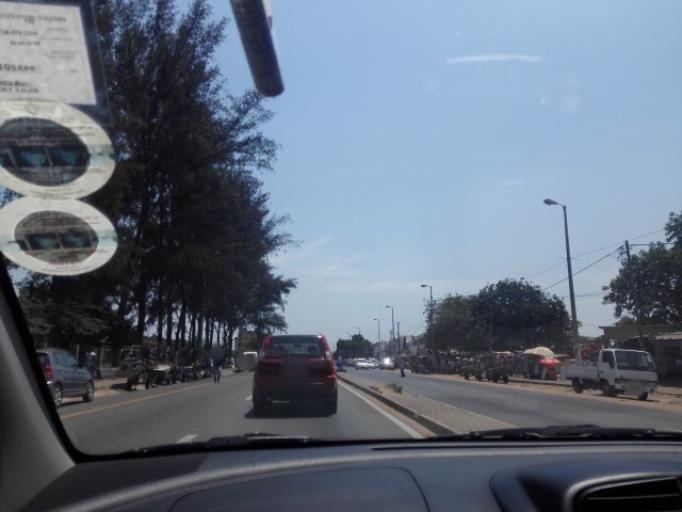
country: MZ
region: Maputo City
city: Maputo
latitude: -25.9329
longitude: 32.5521
